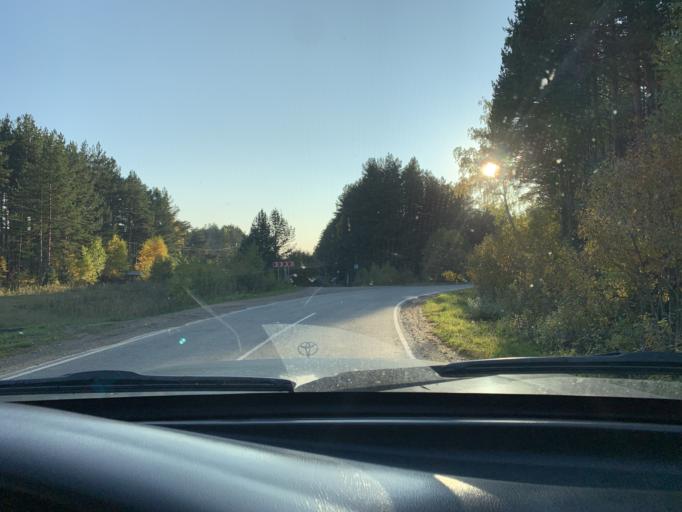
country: RU
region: Sverdlovsk
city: Verkhneye Dubrovo
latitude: 56.8653
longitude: 61.0896
